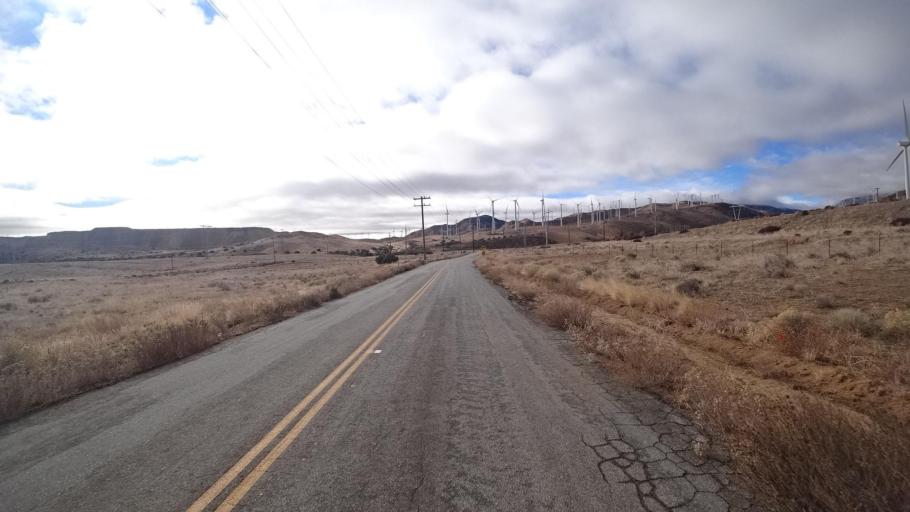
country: US
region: California
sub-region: Kern County
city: Tehachapi
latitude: 35.0556
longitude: -118.3543
